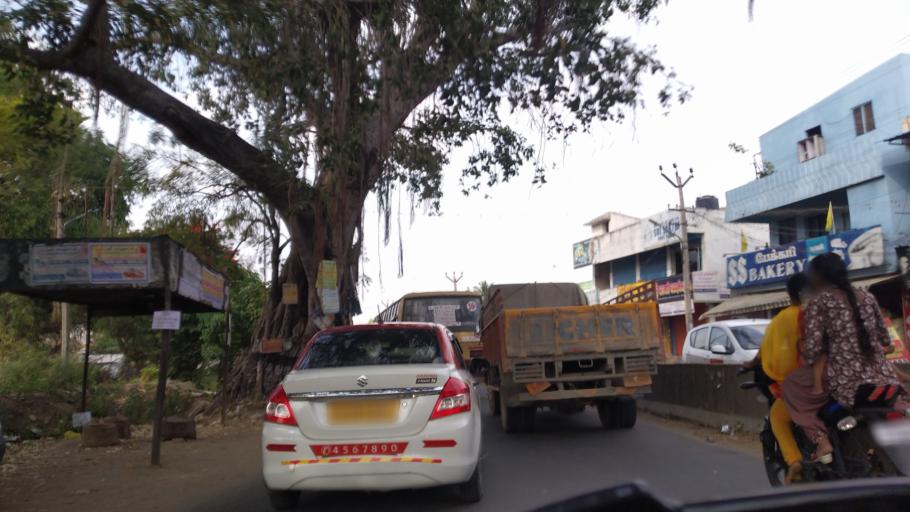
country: IN
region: Tamil Nadu
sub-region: Coimbatore
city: Perur
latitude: 10.9718
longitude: 76.9127
